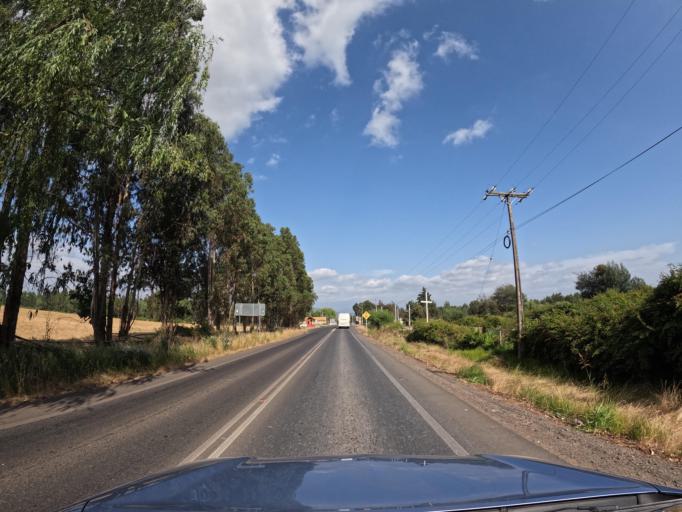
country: CL
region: Maule
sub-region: Provincia de Curico
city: Molina
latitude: -35.2738
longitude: -71.2984
